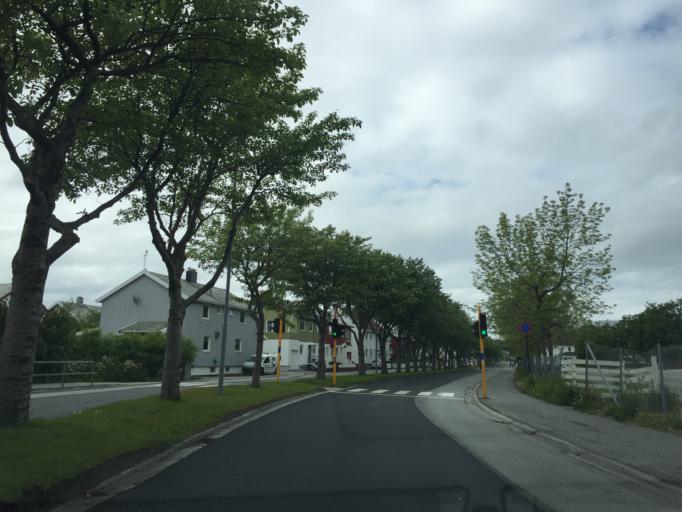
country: NO
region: Nordland
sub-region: Bodo
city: Bodo
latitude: 67.2776
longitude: 14.3806
